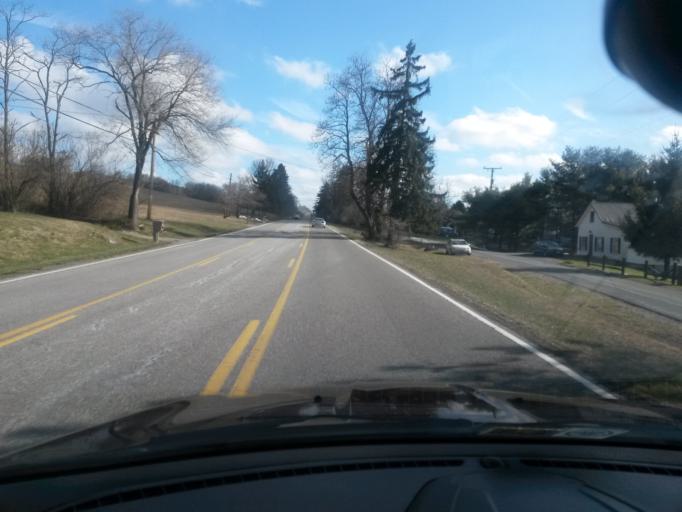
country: US
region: Virginia
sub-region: Augusta County
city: Jolivue
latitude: 38.0658
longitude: -79.1087
